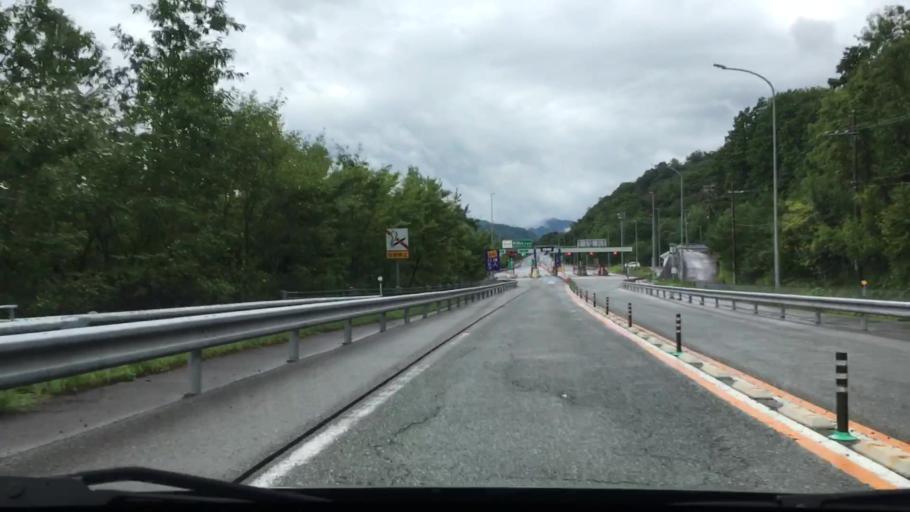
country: JP
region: Hyogo
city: Toyooka
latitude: 35.2881
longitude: 134.8229
